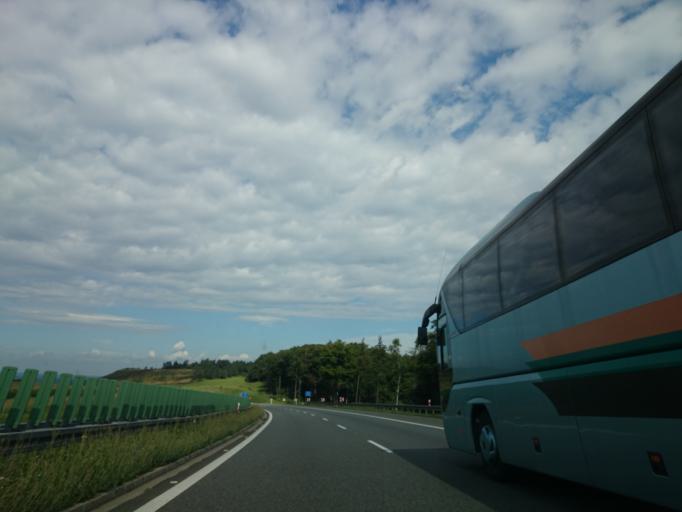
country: PL
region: Opole Voivodeship
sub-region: Powiat krapkowicki
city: Zdzieszowice
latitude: 50.4776
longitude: 18.1354
